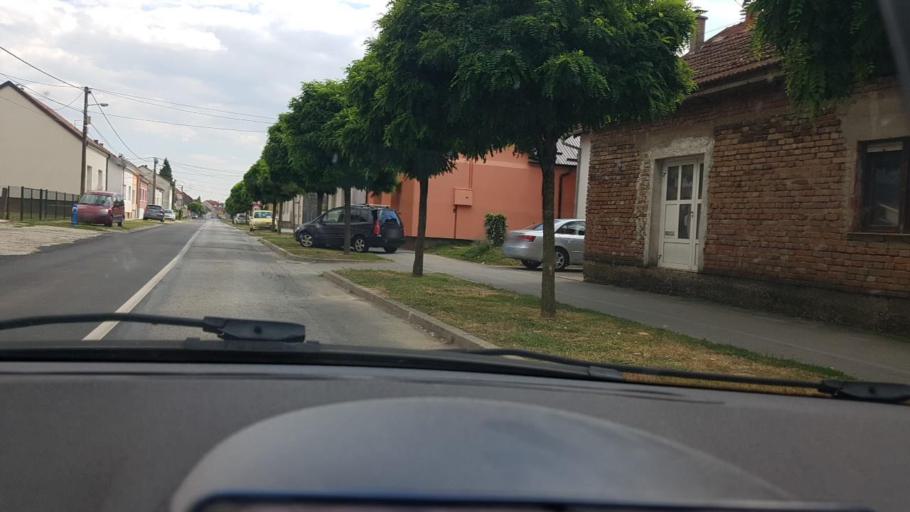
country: HR
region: Bjelovarsko-Bilogorska
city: Bjelovar
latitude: 45.9094
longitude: 16.8464
